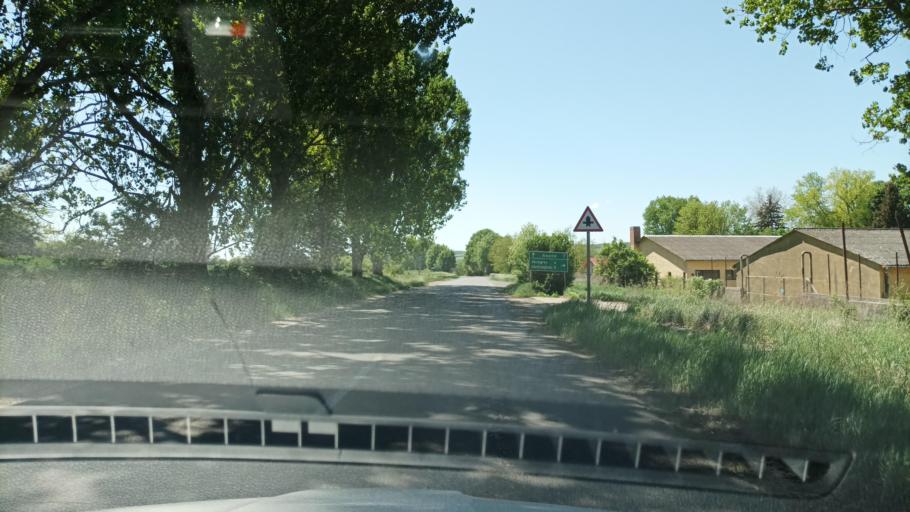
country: HU
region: Pest
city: Galgamacsa
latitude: 47.6916
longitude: 19.4024
